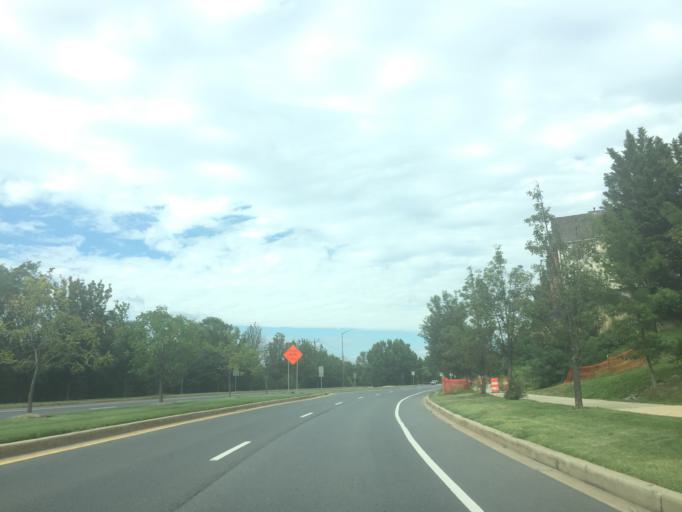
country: US
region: Maryland
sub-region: Montgomery County
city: North Potomac
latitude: 39.1218
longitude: -77.2501
